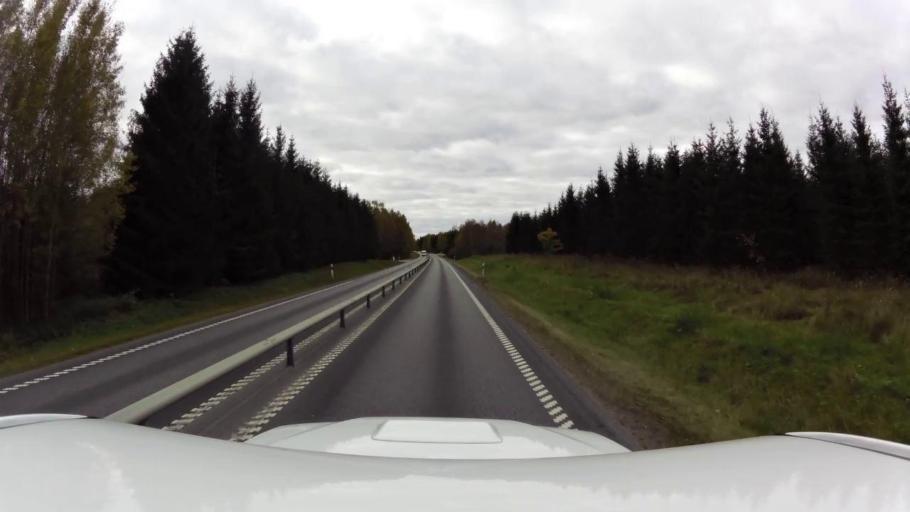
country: SE
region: OEstergoetland
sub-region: Linkopings Kommun
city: Malmslatt
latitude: 58.3864
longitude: 15.5423
